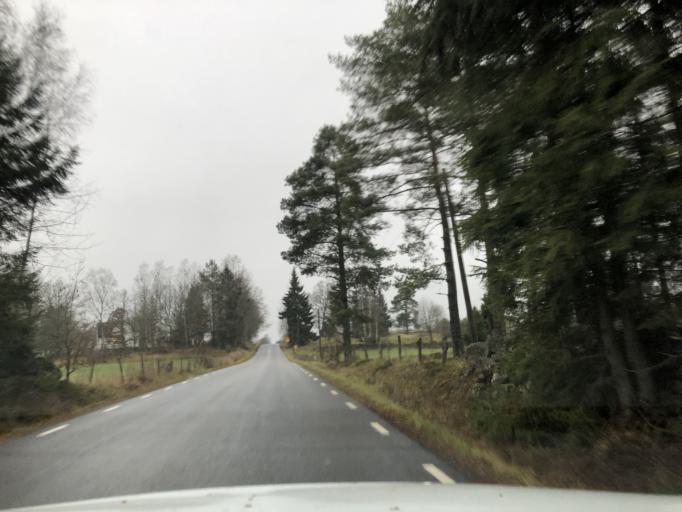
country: SE
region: Vaestra Goetaland
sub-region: Ulricehamns Kommun
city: Ulricehamn
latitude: 57.8343
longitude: 13.3892
